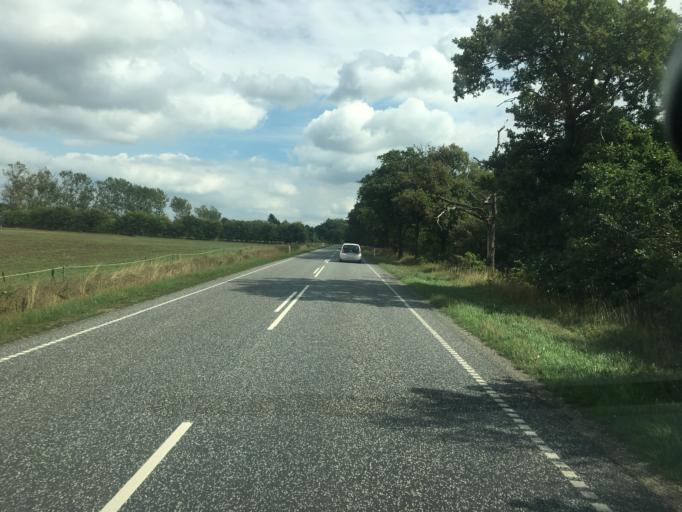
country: DK
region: South Denmark
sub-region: Aabenraa Kommune
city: Aabenraa
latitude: 54.9810
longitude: 9.3659
